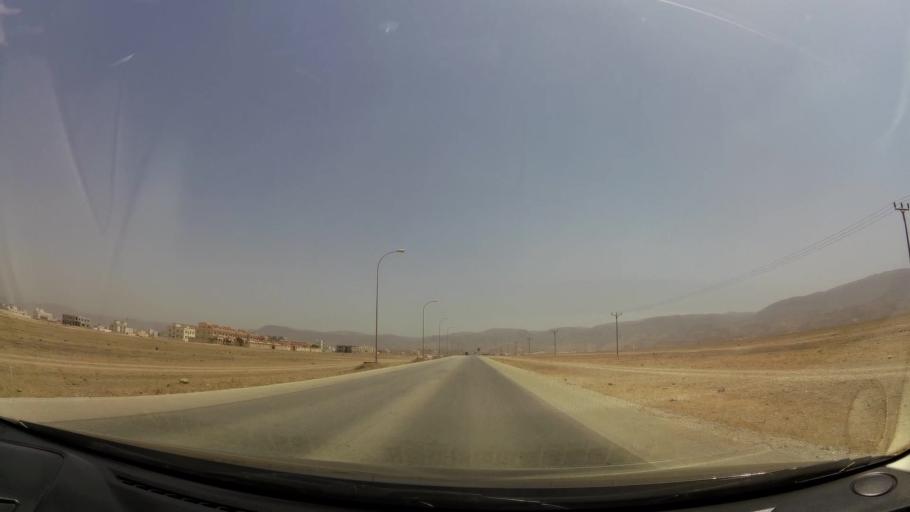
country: OM
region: Zufar
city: Salalah
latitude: 17.0904
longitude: 54.2169
